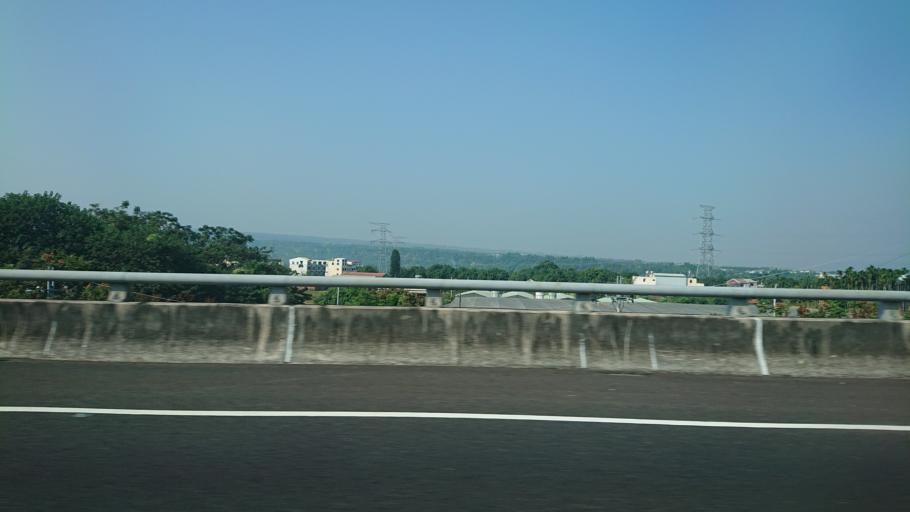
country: TW
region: Taiwan
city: Lugu
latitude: 23.8279
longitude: 120.7082
